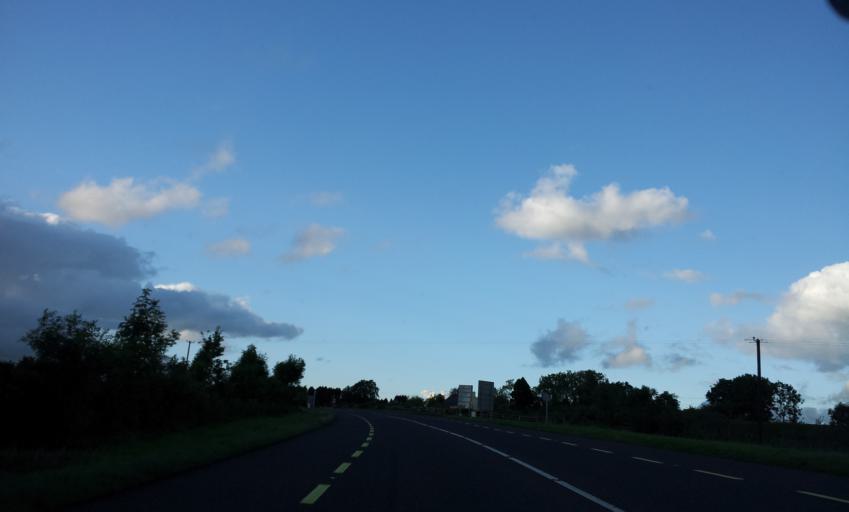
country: IE
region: Munster
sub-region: County Limerick
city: Abbeyfeale
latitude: 52.3572
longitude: -9.3254
